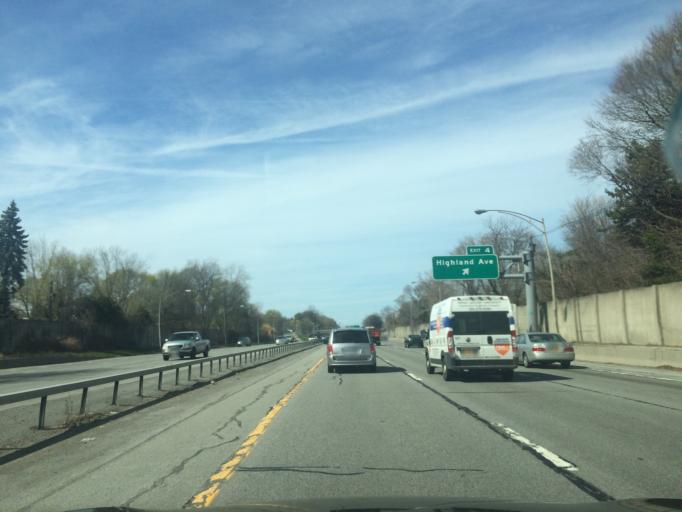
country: US
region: New York
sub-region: Monroe County
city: Brighton
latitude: 43.1328
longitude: -77.5531
